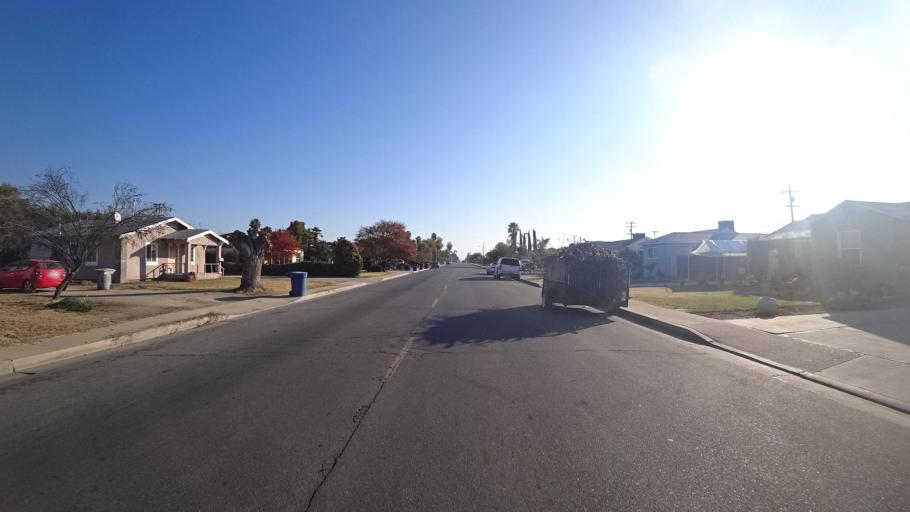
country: US
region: California
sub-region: Kern County
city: Delano
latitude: 35.7676
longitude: -119.2347
